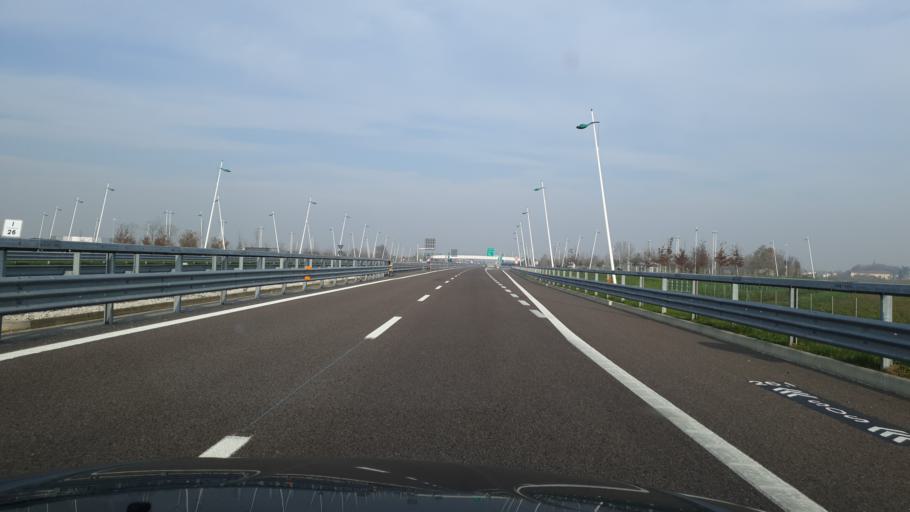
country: IT
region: Veneto
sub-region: Provincia di Vicenza
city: Noventa Vicentina
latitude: 45.2842
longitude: 11.5723
